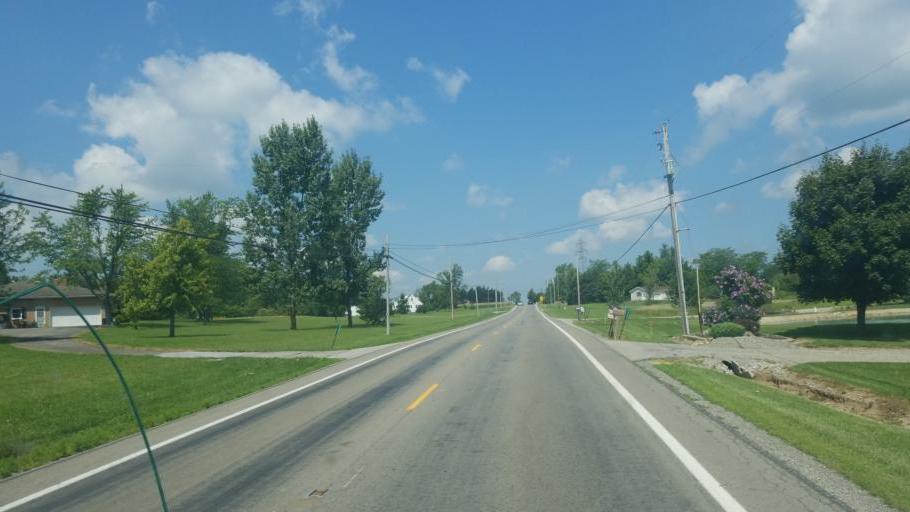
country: US
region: Ohio
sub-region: Allen County
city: Lima
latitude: 40.6992
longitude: -83.9892
